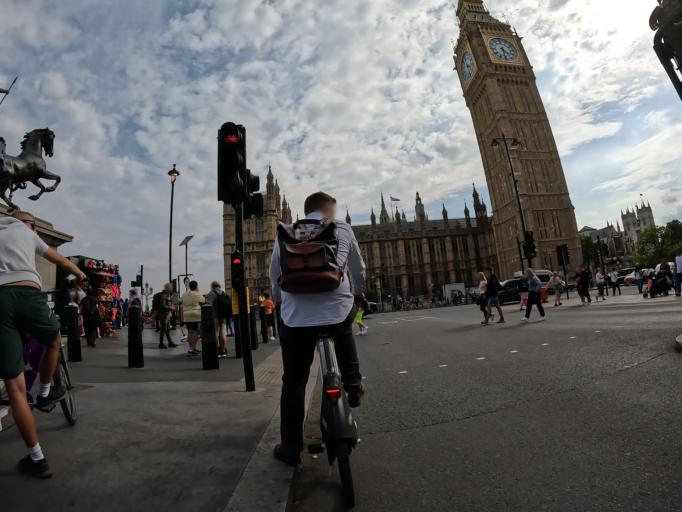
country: GB
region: England
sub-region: Kent
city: Halstead
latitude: 51.3394
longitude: 0.1258
